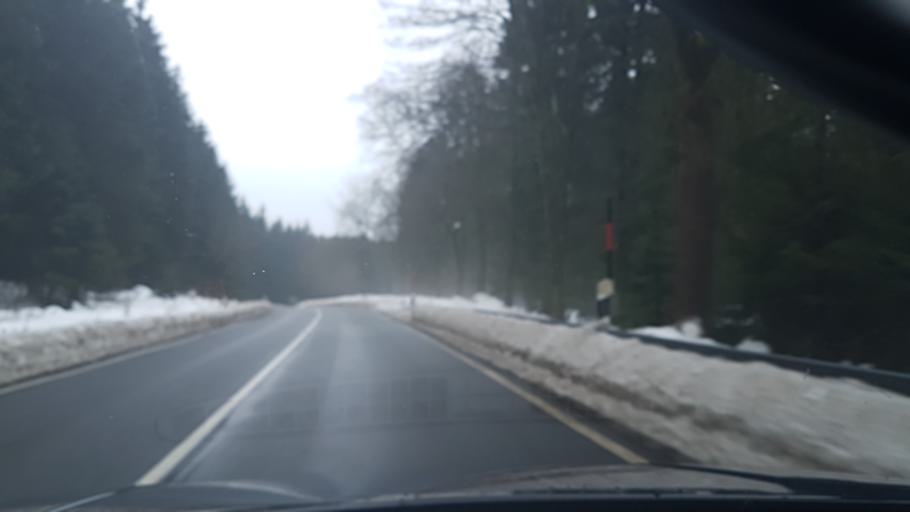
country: DE
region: Lower Saxony
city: Clausthal-Zellerfeld
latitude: 51.8446
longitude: 10.3395
